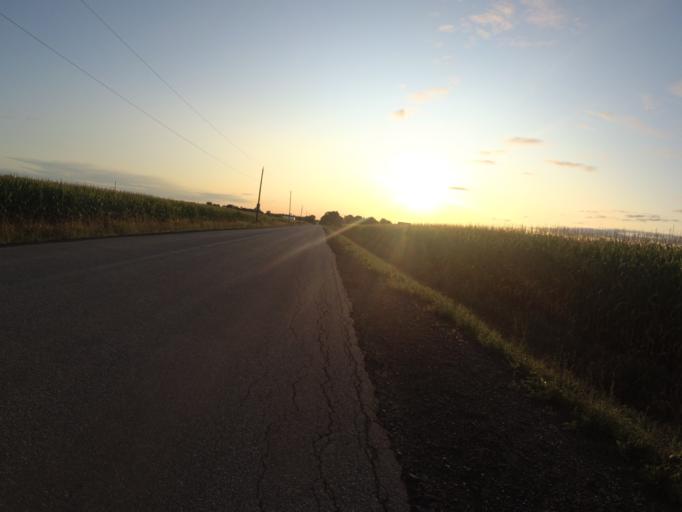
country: CA
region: Ontario
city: Ottawa
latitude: 45.1125
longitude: -75.5300
